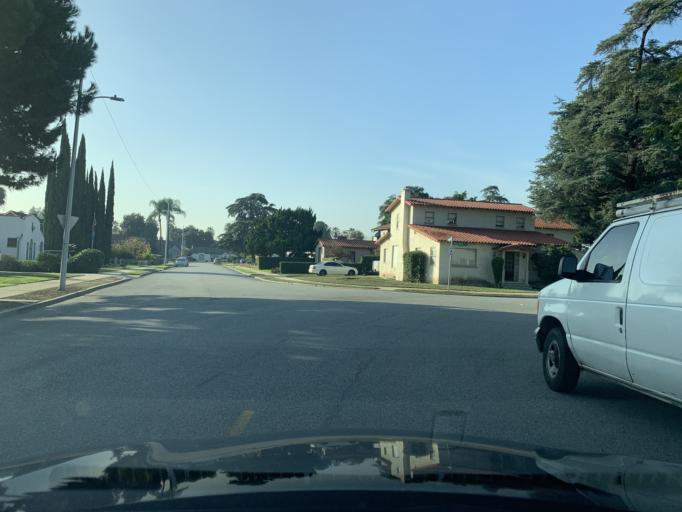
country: US
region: California
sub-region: Los Angeles County
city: Covina
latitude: 34.0872
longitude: -117.8960
